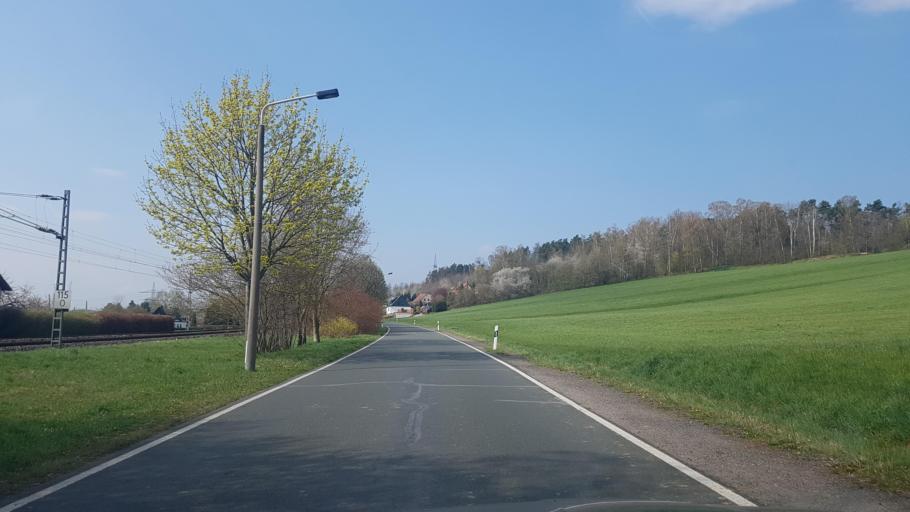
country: DE
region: Saxony
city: Pfaffroda
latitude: 50.8279
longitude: 12.5100
